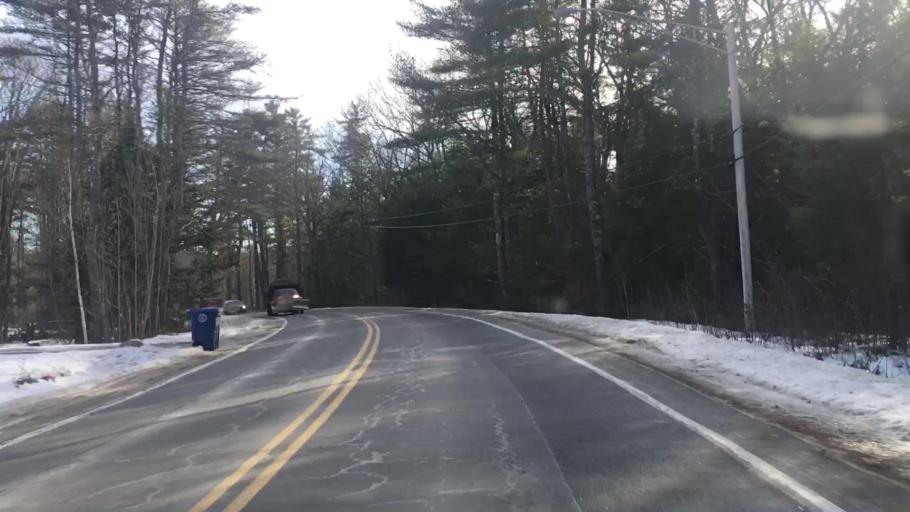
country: US
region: Maine
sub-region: Cumberland County
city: Westbrook
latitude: 43.7275
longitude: -70.3585
